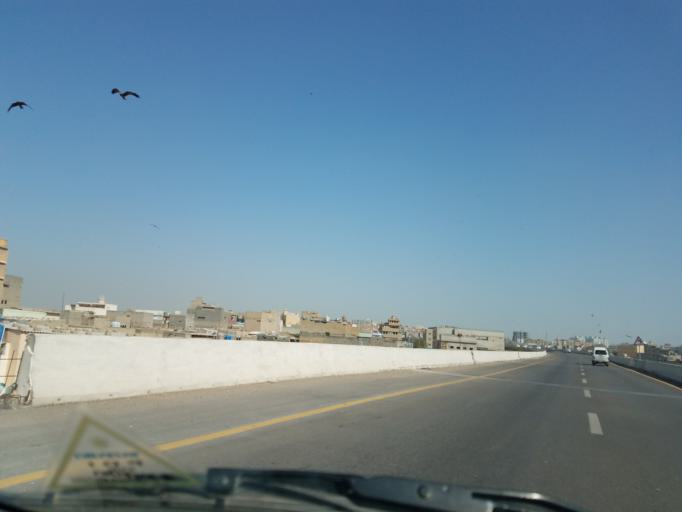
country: PK
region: Sindh
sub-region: Karachi District
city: Karachi
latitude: 24.8809
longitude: 67.0075
